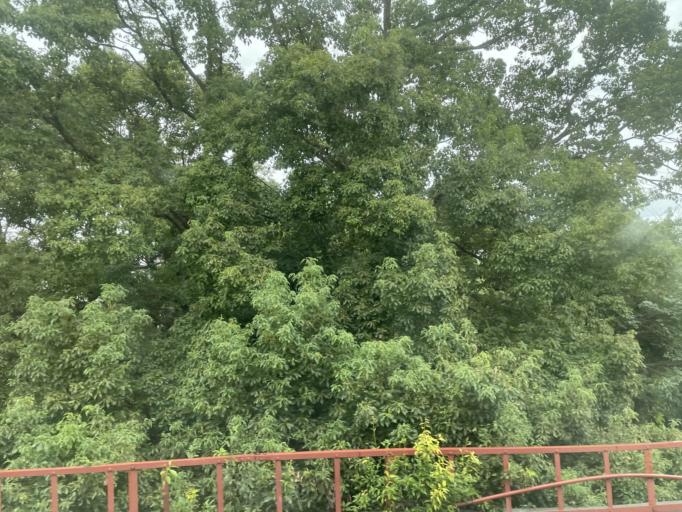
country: JP
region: Wakayama
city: Iwade
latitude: 34.3417
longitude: 135.2631
